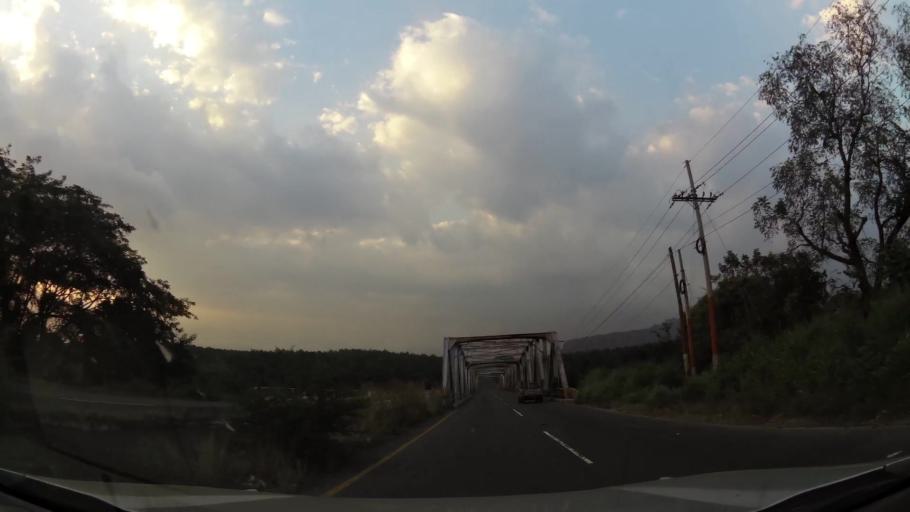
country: GT
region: Escuintla
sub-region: Municipio de La Democracia
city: La Democracia
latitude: 14.2675
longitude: -90.8963
